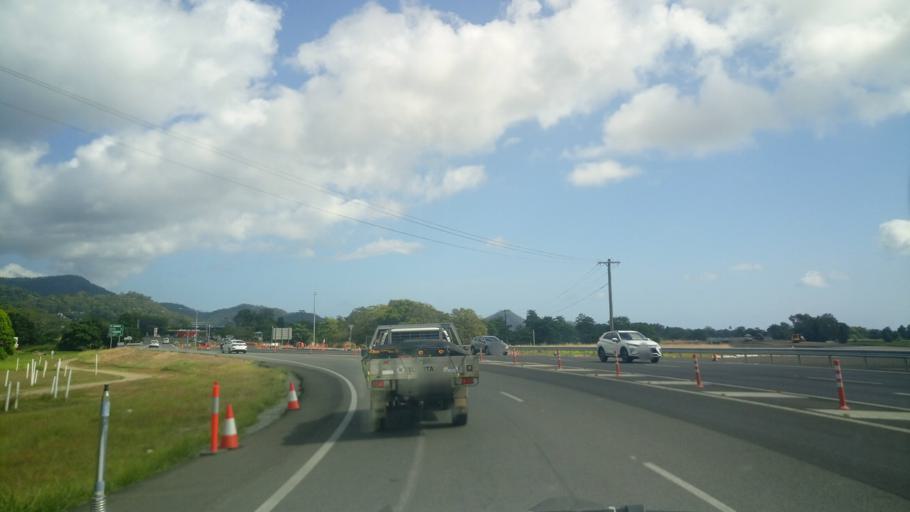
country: AU
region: Queensland
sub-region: Cairns
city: Redlynch
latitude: -16.8471
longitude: 145.6968
